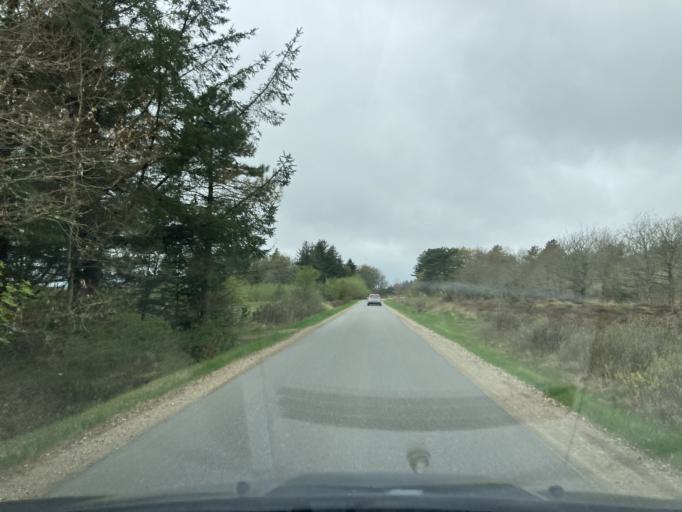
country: DK
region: North Denmark
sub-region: Thisted Kommune
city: Hurup
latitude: 56.8165
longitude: 8.2974
